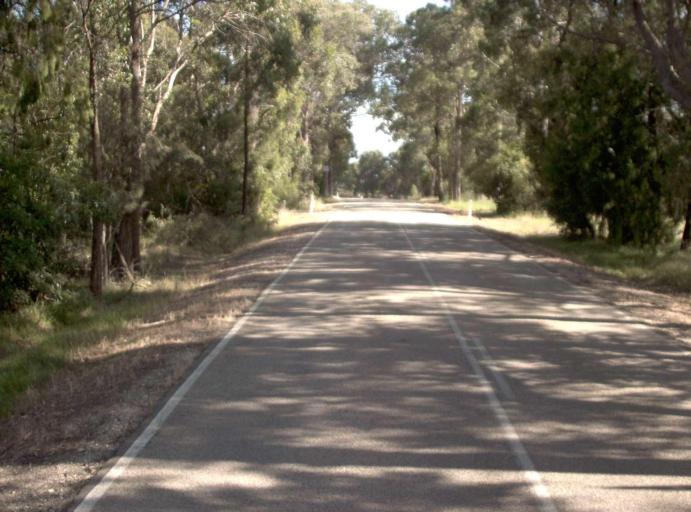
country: AU
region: Victoria
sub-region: East Gippsland
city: Lakes Entrance
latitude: -37.7654
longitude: 147.8124
